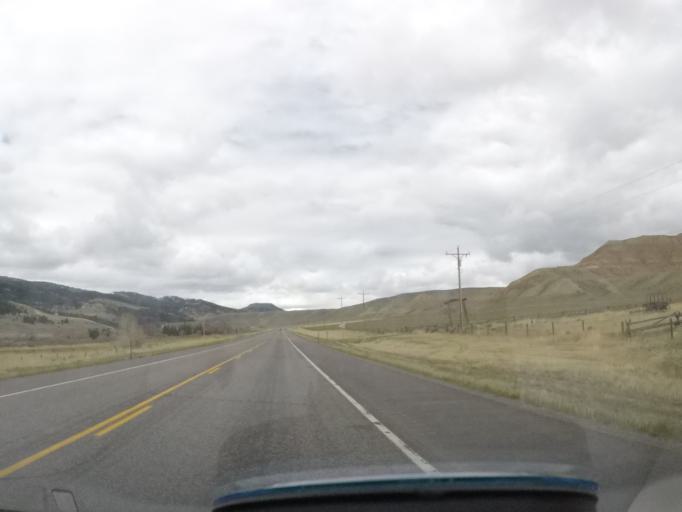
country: US
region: Wyoming
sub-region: Sublette County
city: Pinedale
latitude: 43.5738
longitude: -109.7279
